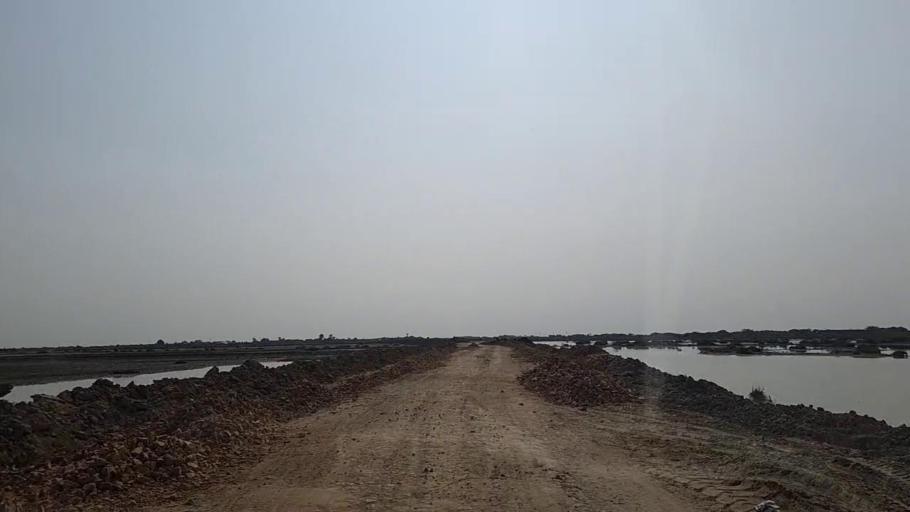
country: PK
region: Sindh
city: Chuhar Jamali
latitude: 24.1984
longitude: 67.8491
